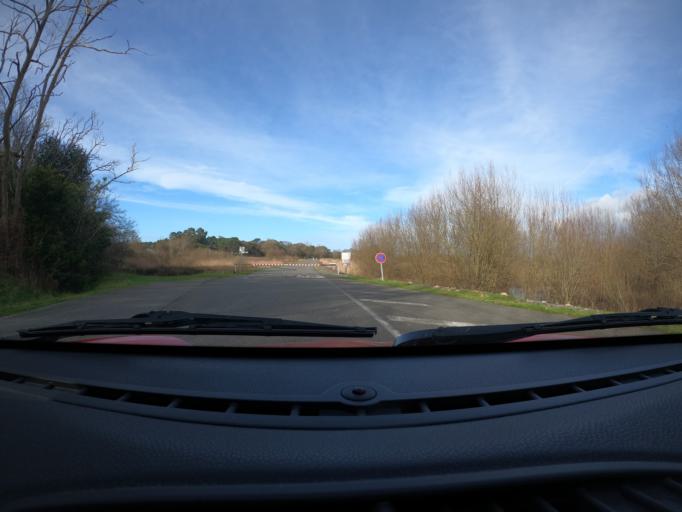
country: FR
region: Aquitaine
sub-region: Departement des Landes
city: Labenne
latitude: 43.5914
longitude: -1.4087
